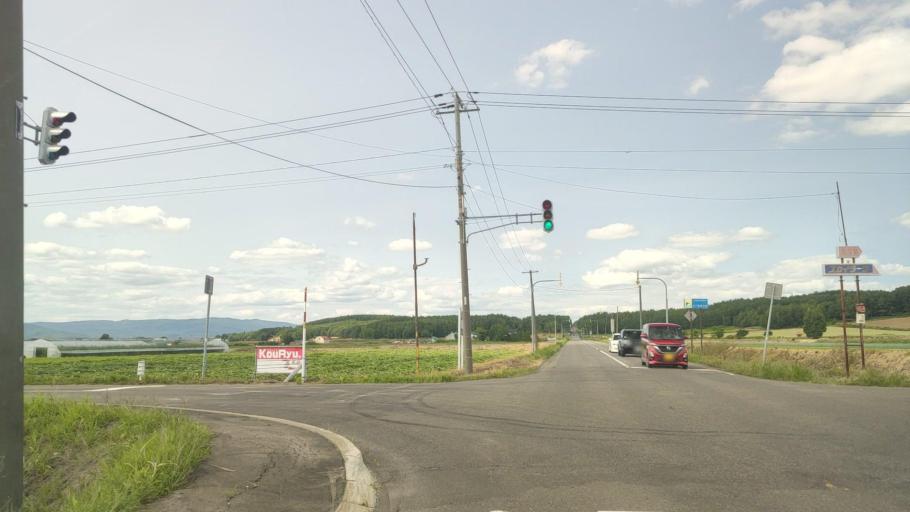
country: JP
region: Hokkaido
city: Nayoro
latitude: 44.2354
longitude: 142.4156
